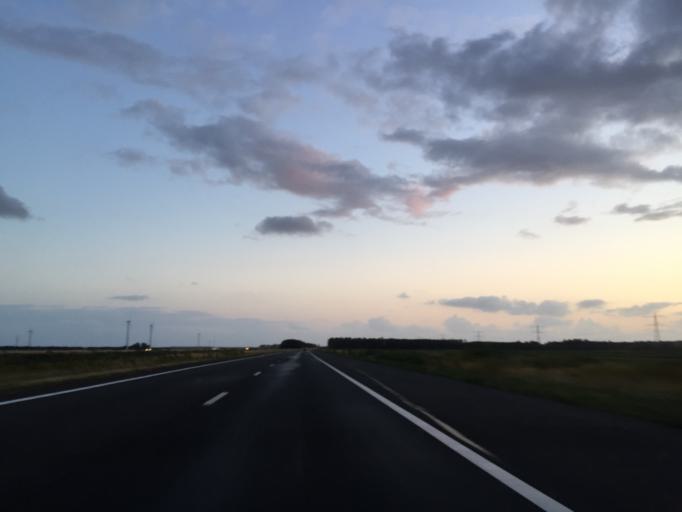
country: NL
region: Flevoland
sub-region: Gemeente Lelystad
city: Lelystad
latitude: 52.4154
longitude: 5.3854
